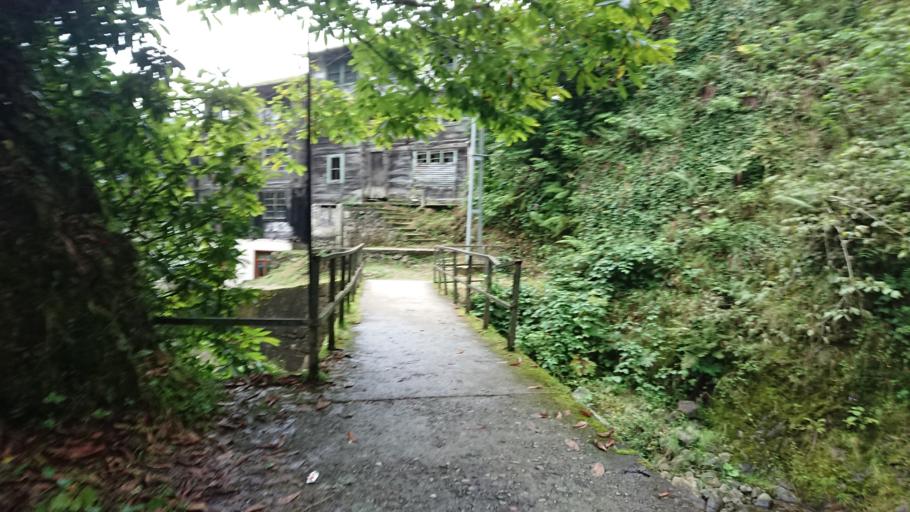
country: TR
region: Rize
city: Ikizdere
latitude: 40.8590
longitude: 40.5868
